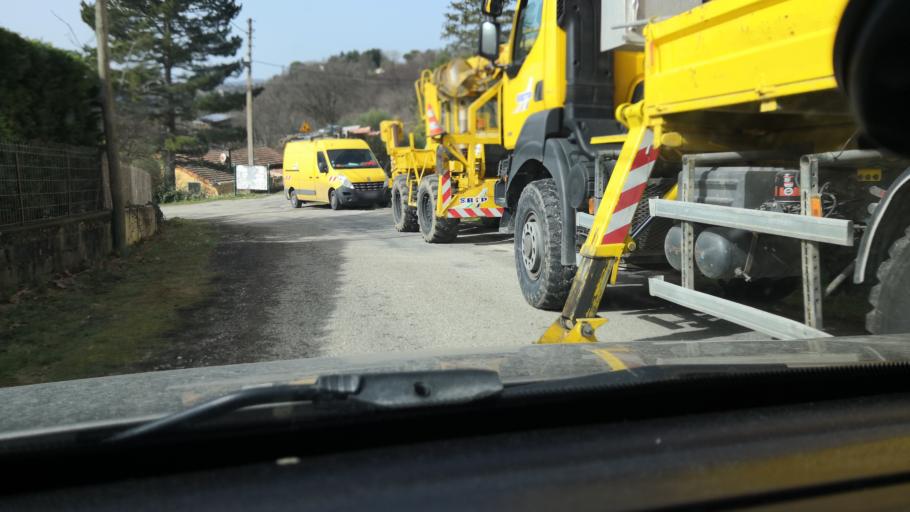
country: FR
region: Rhone-Alpes
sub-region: Departement de la Drome
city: Dieulefit
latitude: 44.5214
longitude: 5.0728
